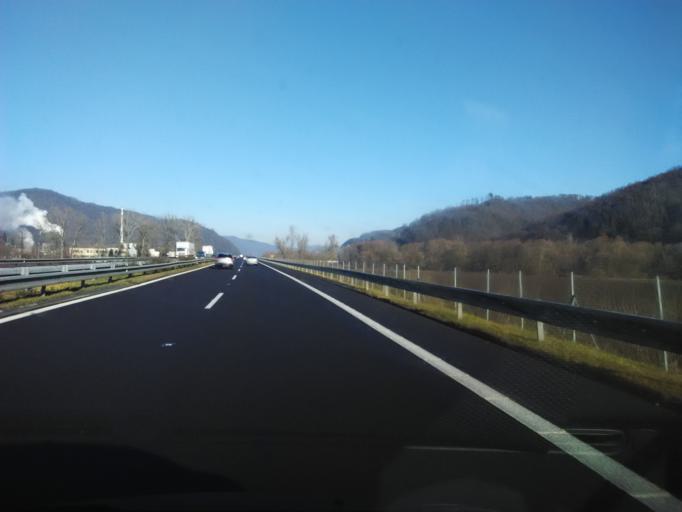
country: SK
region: Banskobystricky
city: Zarnovica
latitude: 48.4790
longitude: 18.7298
